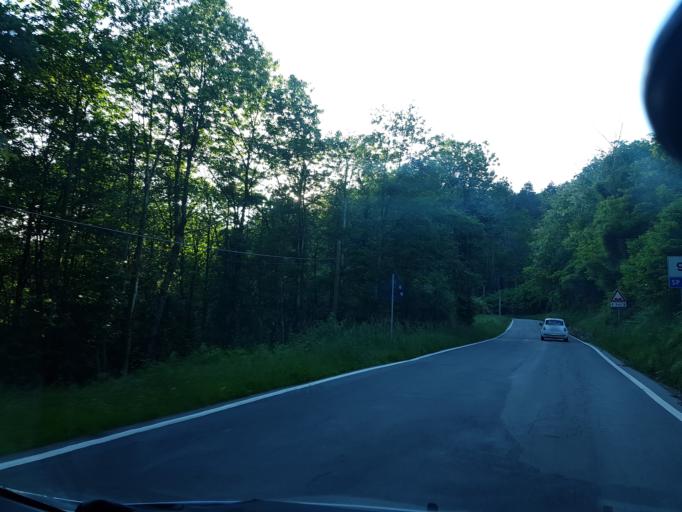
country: IT
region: Tuscany
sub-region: Provincia di Lucca
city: Minucciano
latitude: 44.1639
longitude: 10.2168
